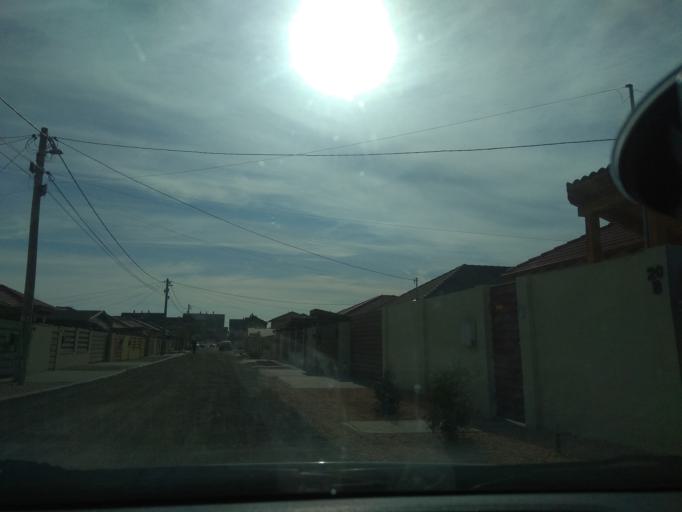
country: HU
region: Pest
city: Szigetszentmiklos
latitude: 47.3627
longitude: 19.0300
